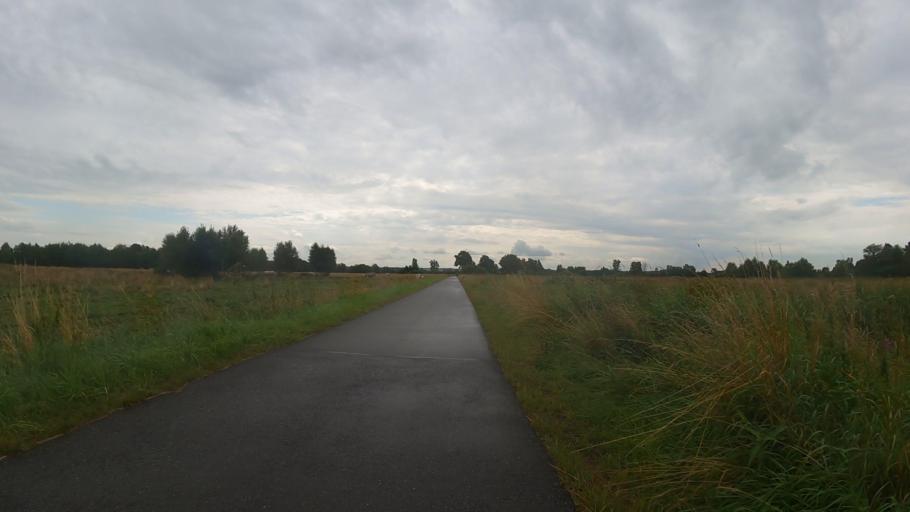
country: DE
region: Lower Saxony
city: Neu Wulmstorf
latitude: 53.4834
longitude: 9.7673
